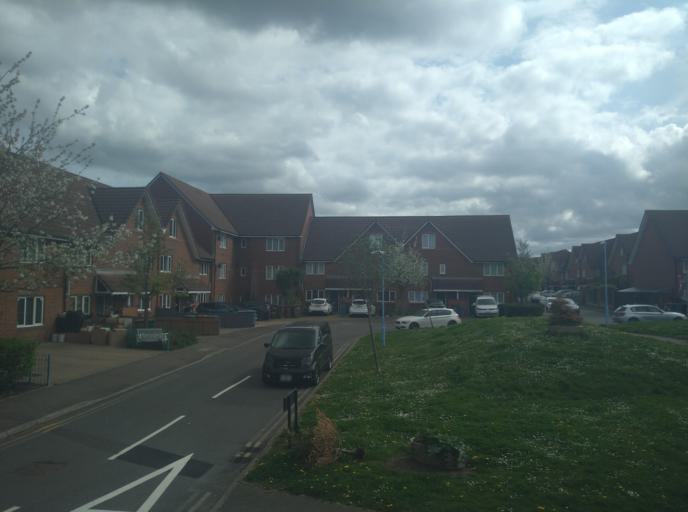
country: GB
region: England
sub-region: Greater London
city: Purley
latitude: 51.3539
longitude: -0.1292
